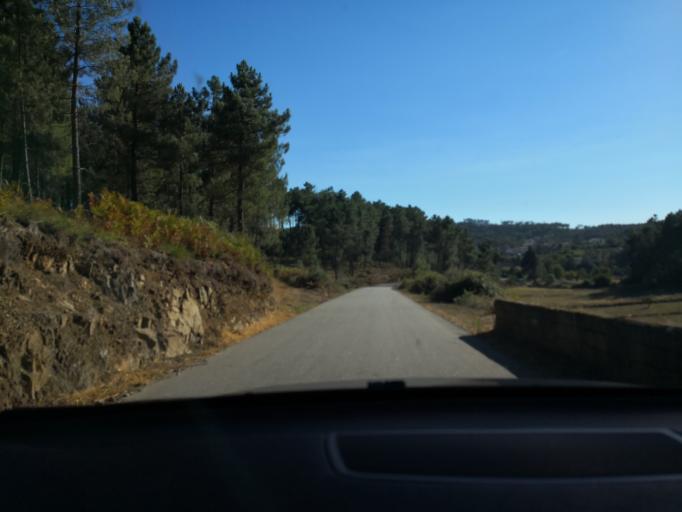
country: PT
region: Vila Real
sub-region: Sabrosa
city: Vilela
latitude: 41.2423
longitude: -7.6113
